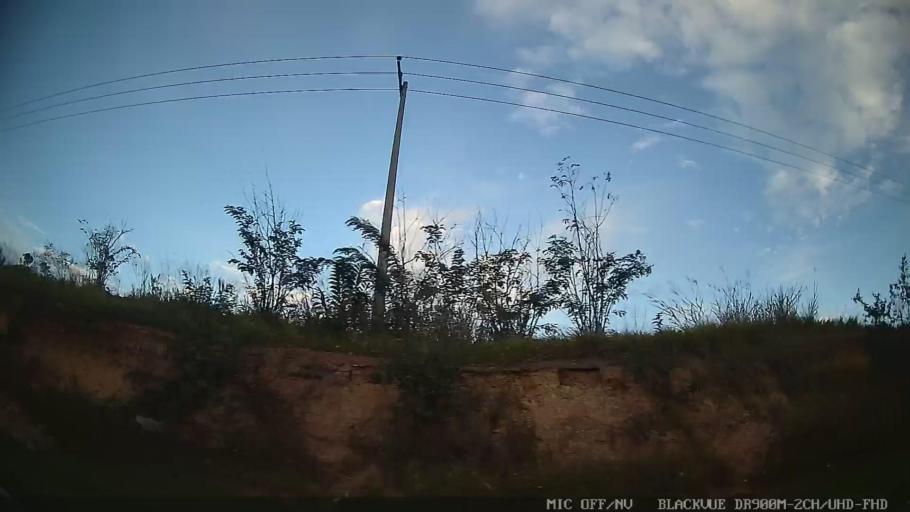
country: BR
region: Sao Paulo
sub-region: Salto
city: Salto
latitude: -23.1599
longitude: -47.2620
